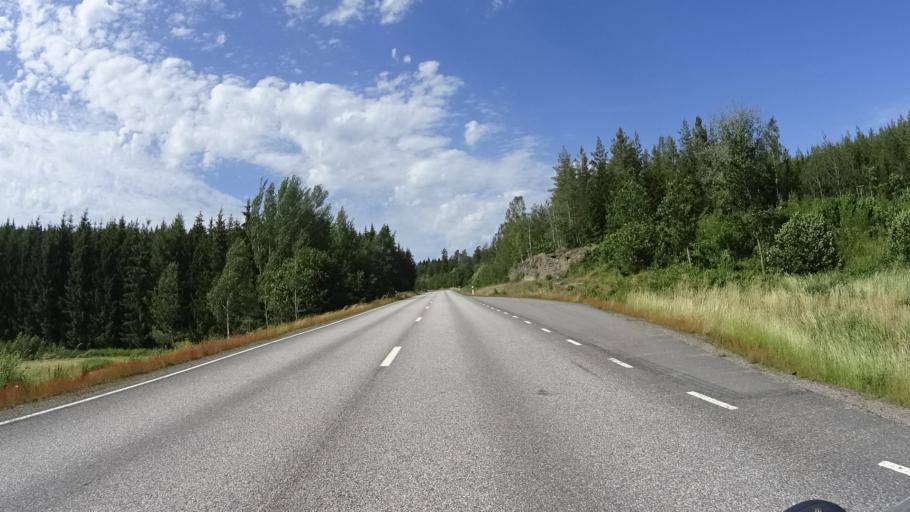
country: SE
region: Kalmar
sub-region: Vasterviks Kommun
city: Overum
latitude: 58.0683
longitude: 16.2010
